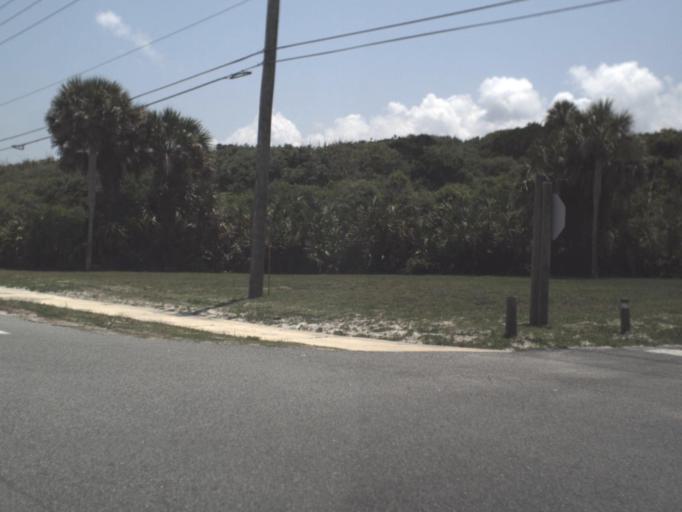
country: US
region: Florida
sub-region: Saint Johns County
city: Butler Beach
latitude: 29.7169
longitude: -81.2329
